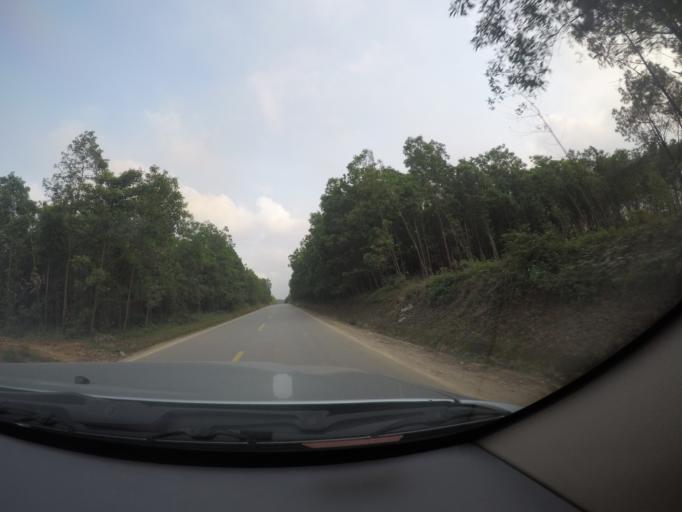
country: VN
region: Quang Binh
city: Kien Giang
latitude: 17.1167
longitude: 106.8307
